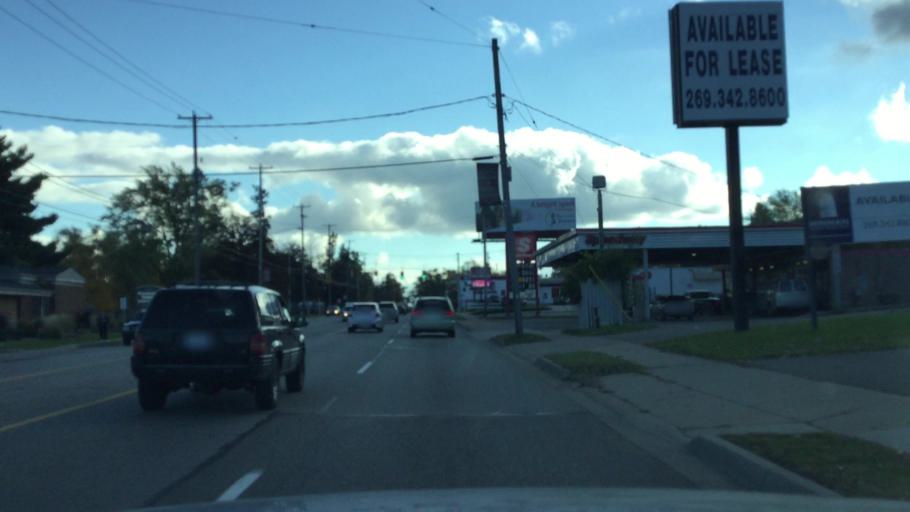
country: US
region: Michigan
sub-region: Kalamazoo County
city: Kalamazoo
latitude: 42.2532
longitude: -85.5897
